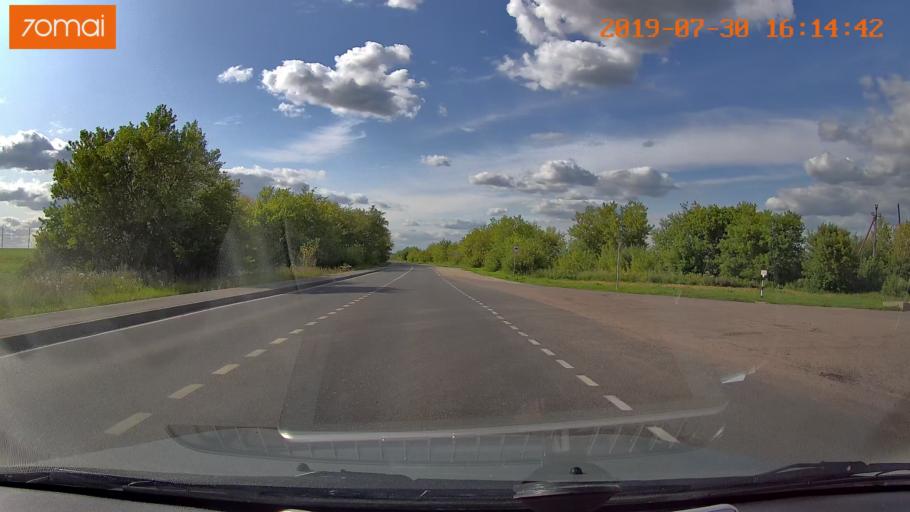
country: RU
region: Moskovskaya
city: Voskresensk
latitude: 55.2912
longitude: 38.6762
